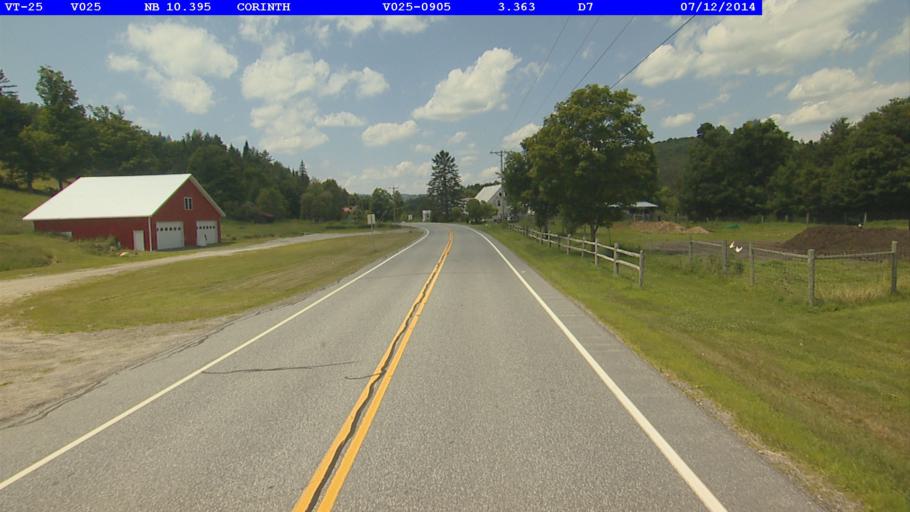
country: US
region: New Hampshire
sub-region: Grafton County
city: Haverhill
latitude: 44.0733
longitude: -72.2511
